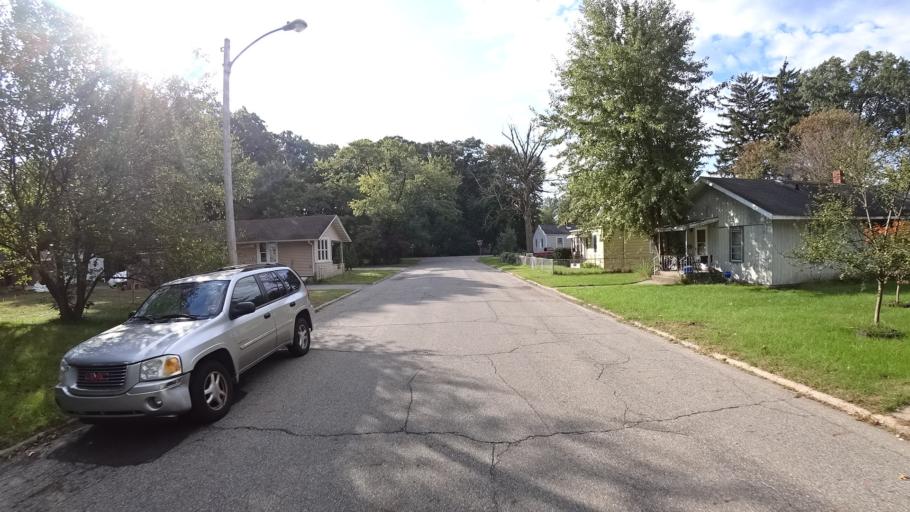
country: US
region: Indiana
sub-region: LaPorte County
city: Trail Creek
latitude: 41.7027
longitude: -86.8726
